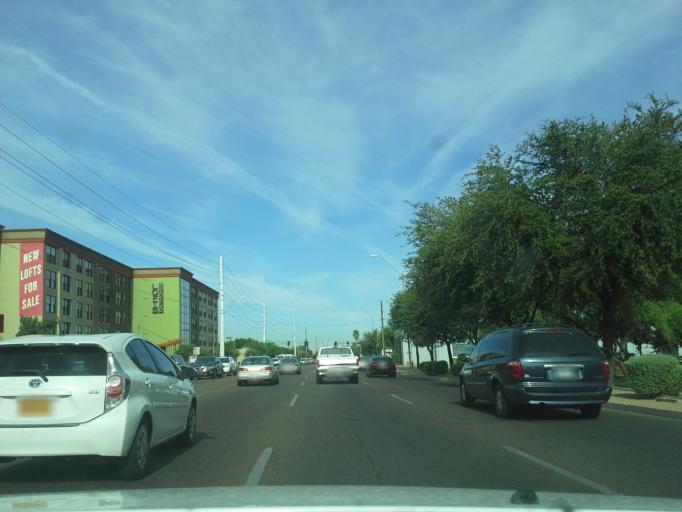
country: US
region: Arizona
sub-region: Maricopa County
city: Phoenix
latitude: 33.4804
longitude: -112.0809
